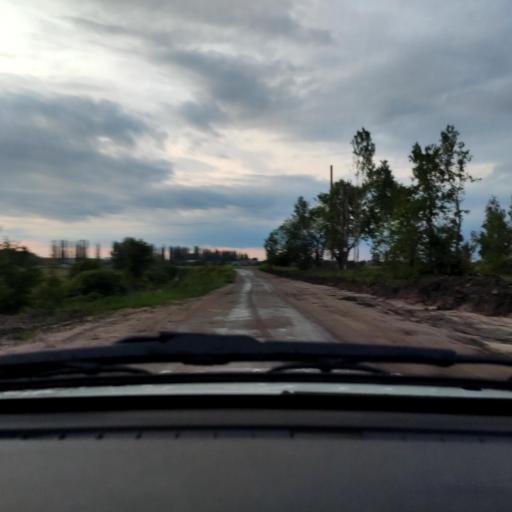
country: RU
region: Voronezj
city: Maslovka
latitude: 51.5145
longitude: 39.2273
